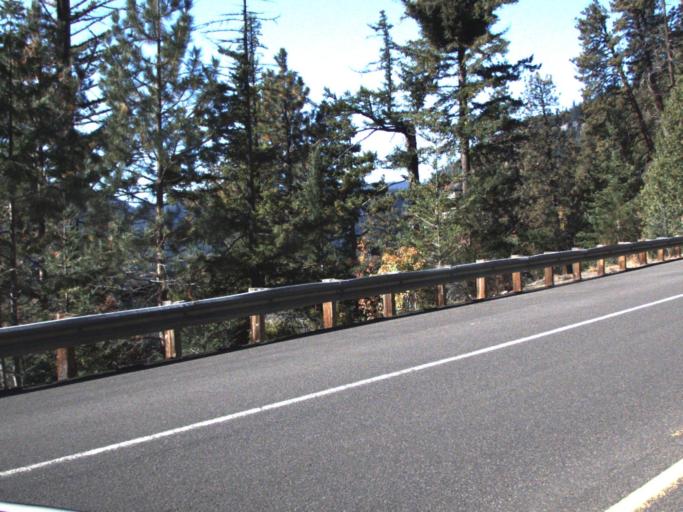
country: US
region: Washington
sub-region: Yakima County
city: Tieton
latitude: 46.6566
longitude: -121.3080
